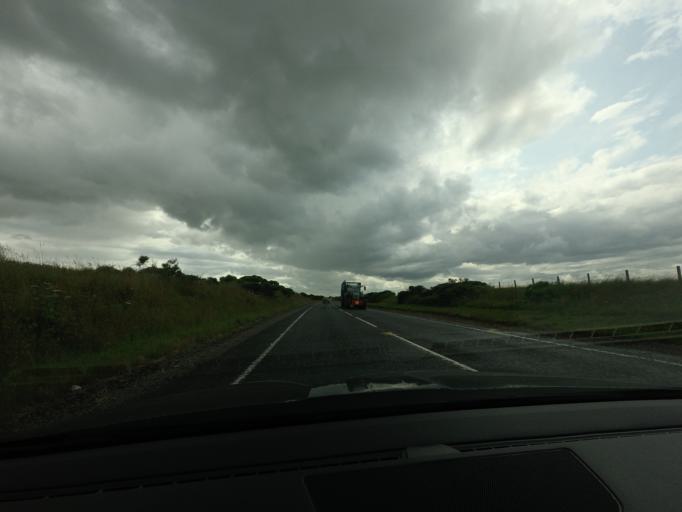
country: GB
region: Scotland
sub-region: Highland
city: Fortrose
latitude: 57.5360
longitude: -4.0266
